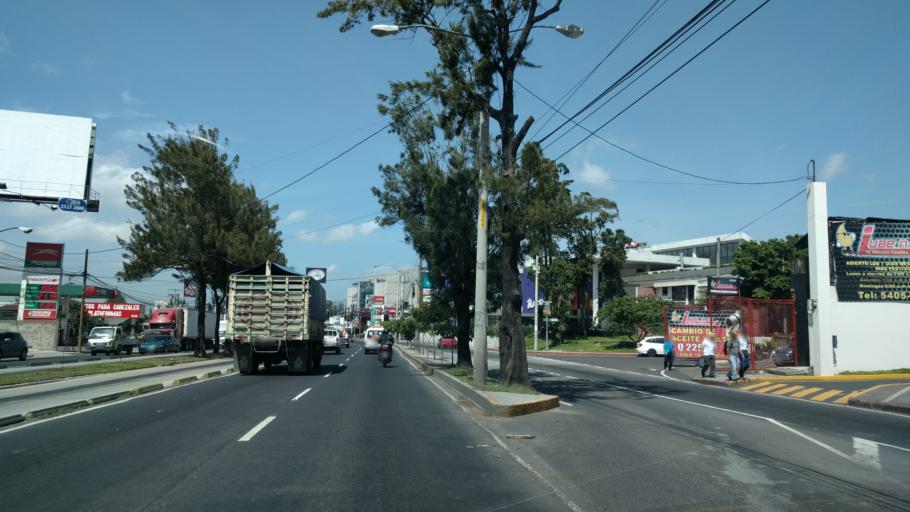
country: GT
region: Guatemala
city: Mixco
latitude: 14.5952
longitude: -90.5571
